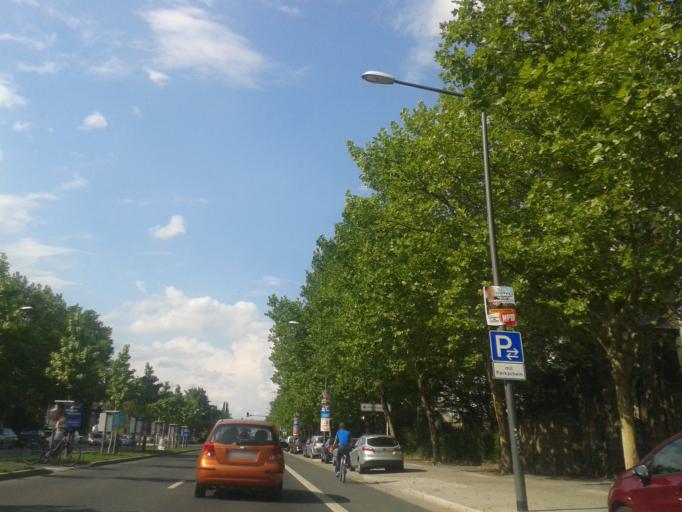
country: DE
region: Saxony
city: Albertstadt
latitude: 51.0547
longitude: 13.7779
